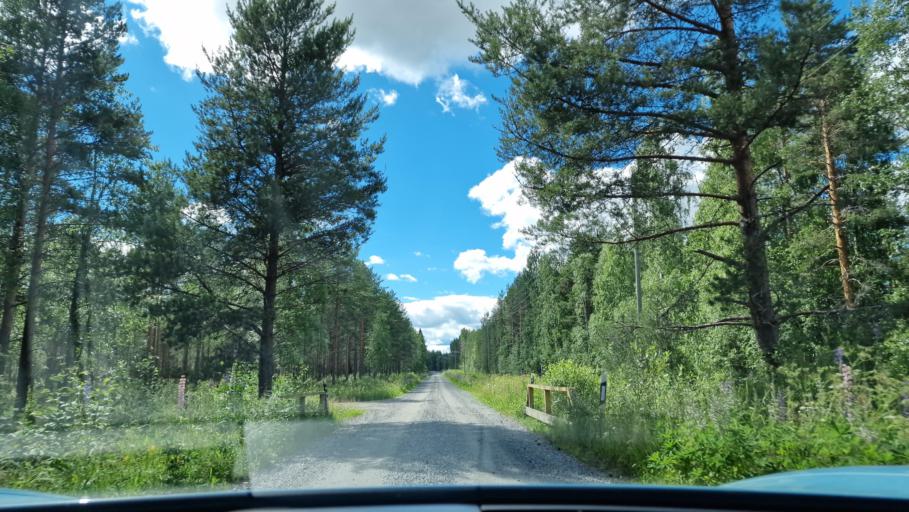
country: FI
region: Southern Ostrobothnia
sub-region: Jaerviseutu
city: Soini
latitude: 62.8467
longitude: 24.3320
